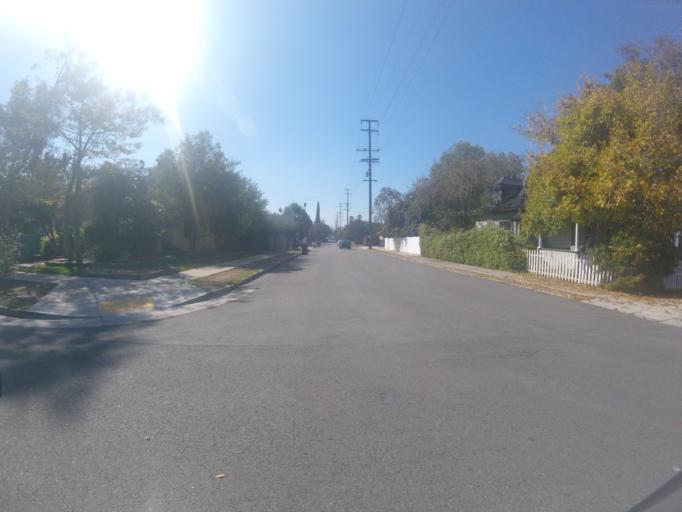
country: US
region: California
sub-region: San Bernardino County
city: Redlands
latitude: 34.0535
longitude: -117.1769
